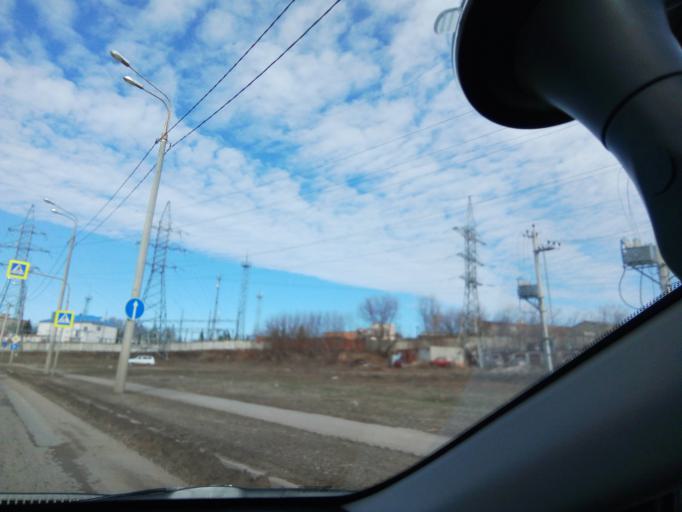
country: RU
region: Chuvashia
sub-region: Cheboksarskiy Rayon
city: Cheboksary
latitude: 56.1092
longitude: 47.2463
